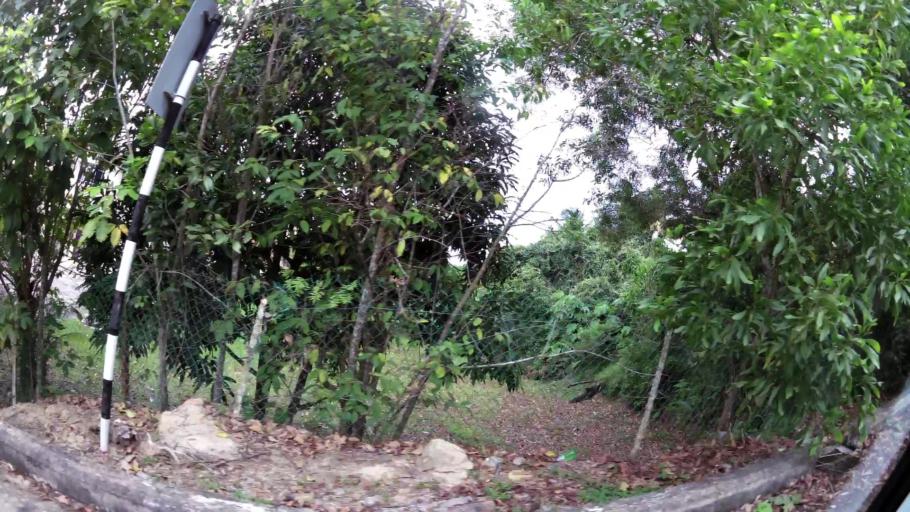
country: BN
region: Brunei and Muara
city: Bandar Seri Begawan
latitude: 4.8819
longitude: 114.8964
